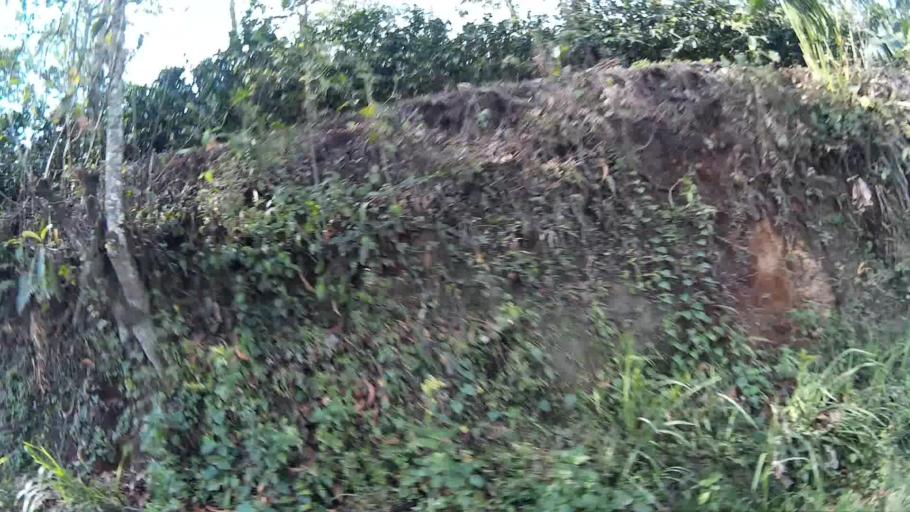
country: CO
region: Valle del Cauca
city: Ulloa
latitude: 4.7146
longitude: -75.7206
